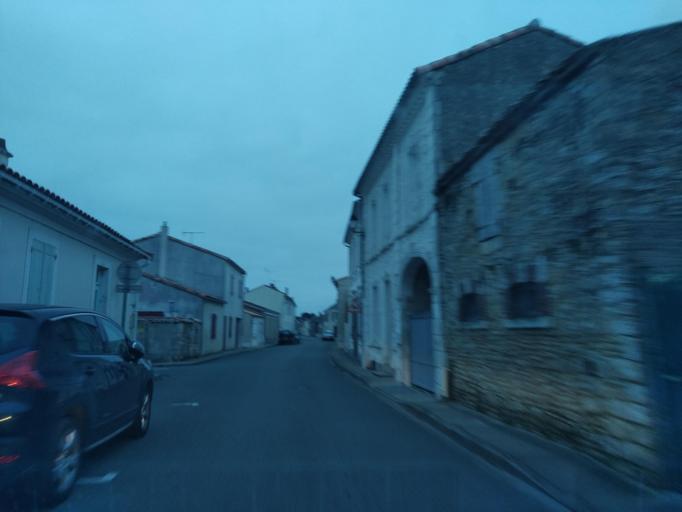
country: FR
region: Pays de la Loire
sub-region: Departement de la Vendee
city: Triaize
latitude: 46.3551
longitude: -1.2497
